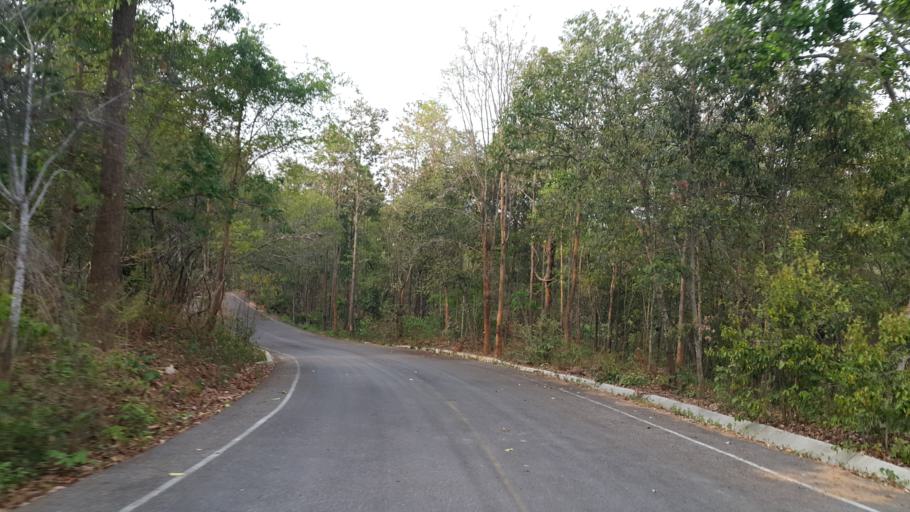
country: TH
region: Chiang Mai
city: Mae On
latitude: 18.7749
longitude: 99.2896
